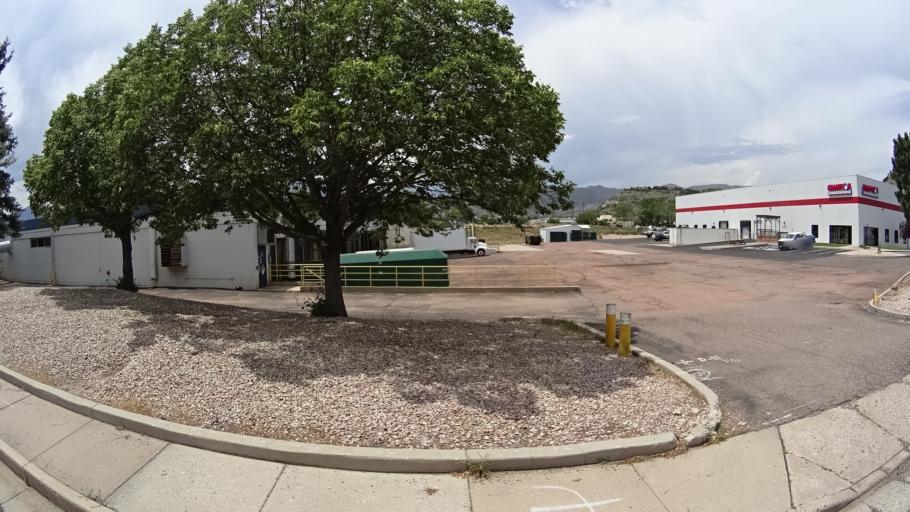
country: US
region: Colorado
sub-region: El Paso County
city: Colorado Springs
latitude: 38.8988
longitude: -104.8358
